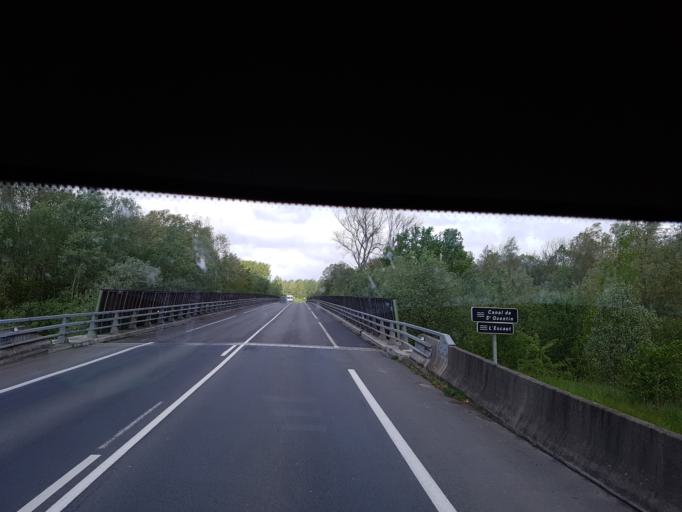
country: FR
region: Nord-Pas-de-Calais
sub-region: Departement du Nord
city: Proville
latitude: 50.1573
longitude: 3.1887
